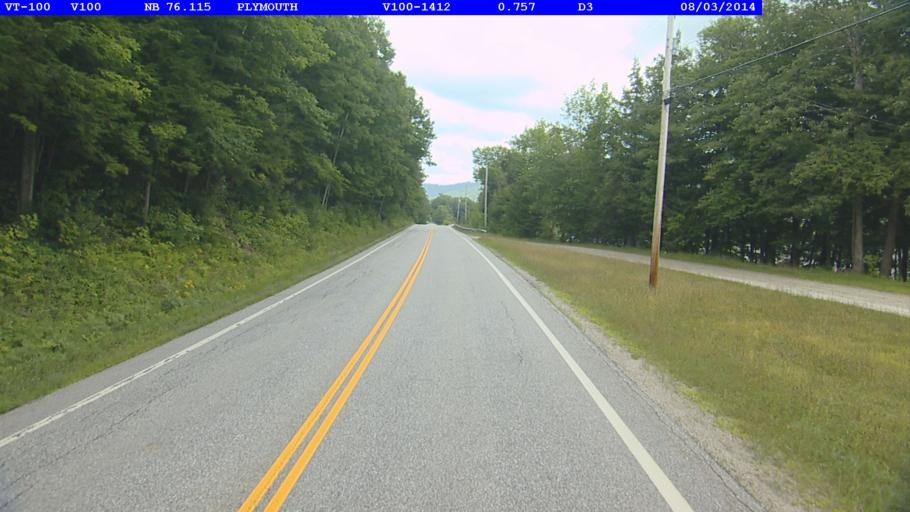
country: US
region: Vermont
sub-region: Windsor County
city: Chester
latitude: 43.4735
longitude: -72.7029
